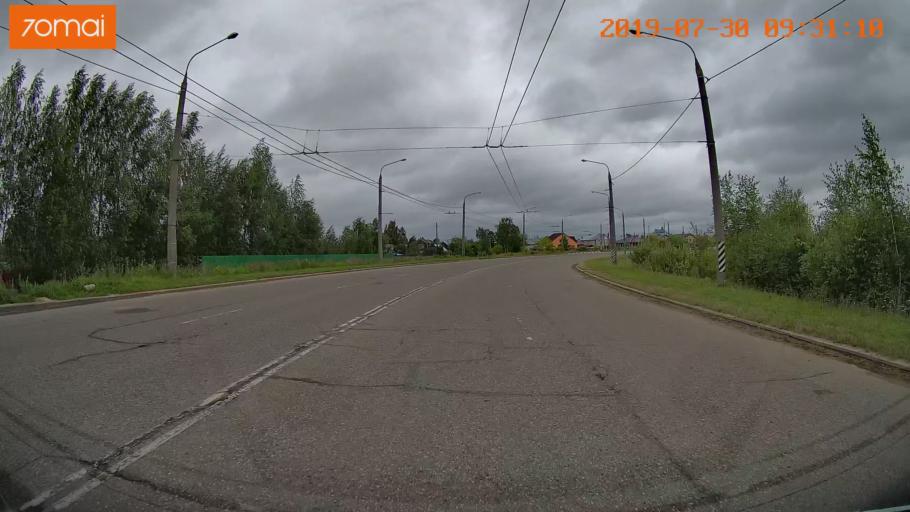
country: RU
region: Ivanovo
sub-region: Gorod Ivanovo
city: Ivanovo
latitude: 56.9526
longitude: 40.9498
